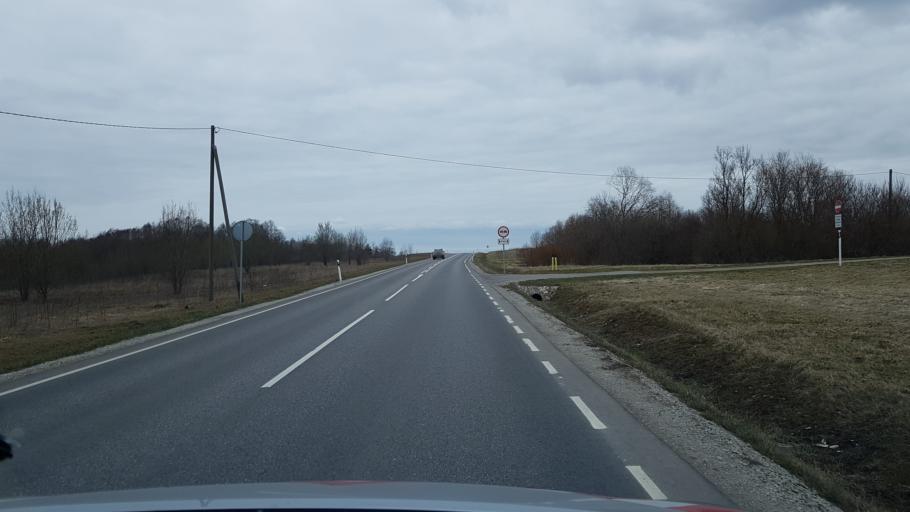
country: EE
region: Ida-Virumaa
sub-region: Narva-Joesuu linn
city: Narva-Joesuu
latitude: 59.4043
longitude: 28.0666
